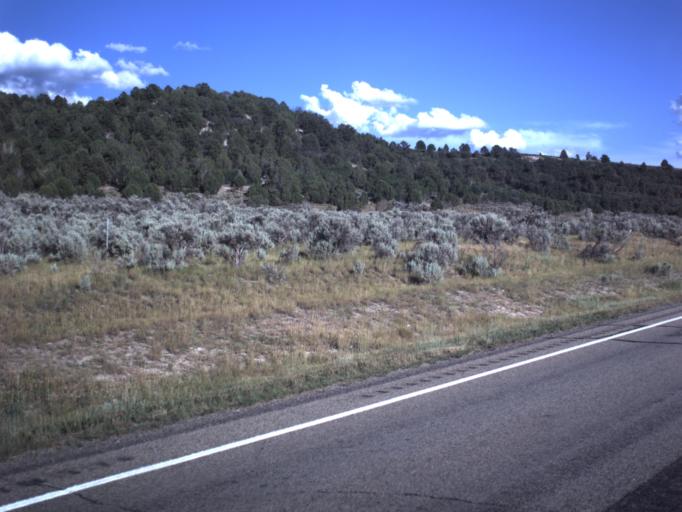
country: US
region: Utah
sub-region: Sanpete County
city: Fairview
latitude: 39.7295
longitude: -111.4753
